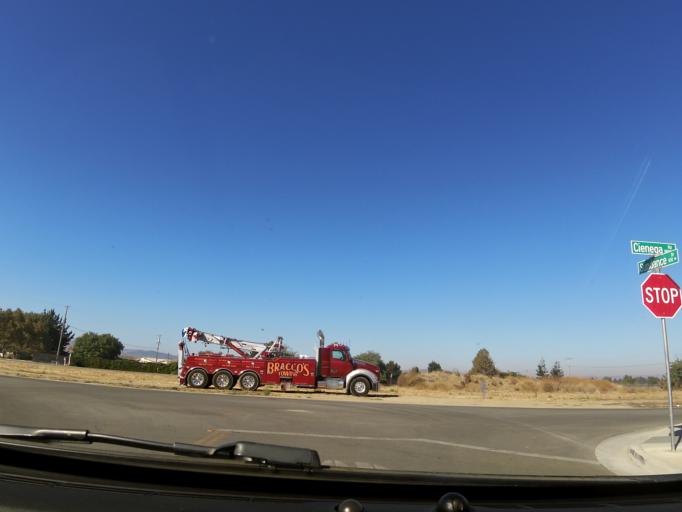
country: US
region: California
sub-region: San Benito County
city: Hollister
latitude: 36.8326
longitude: -121.4008
